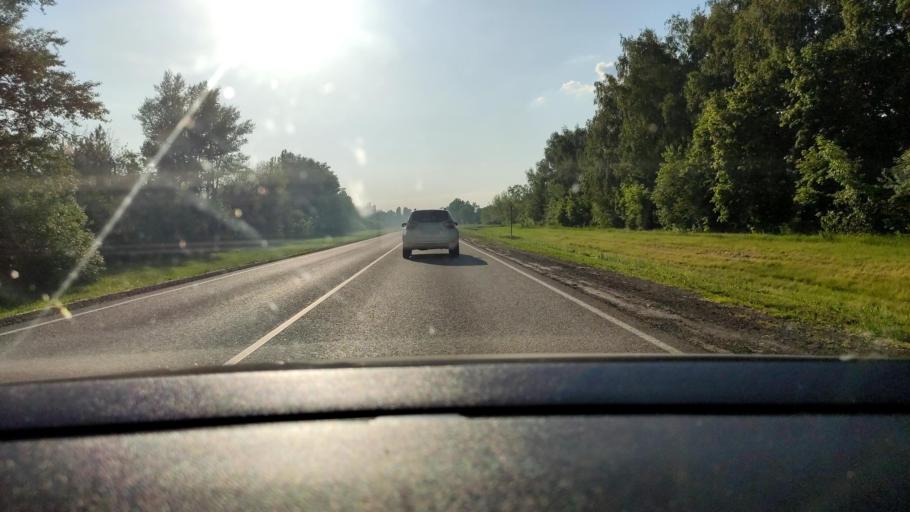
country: RU
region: Voronezj
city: Kashirskoye
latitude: 51.4733
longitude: 39.6854
